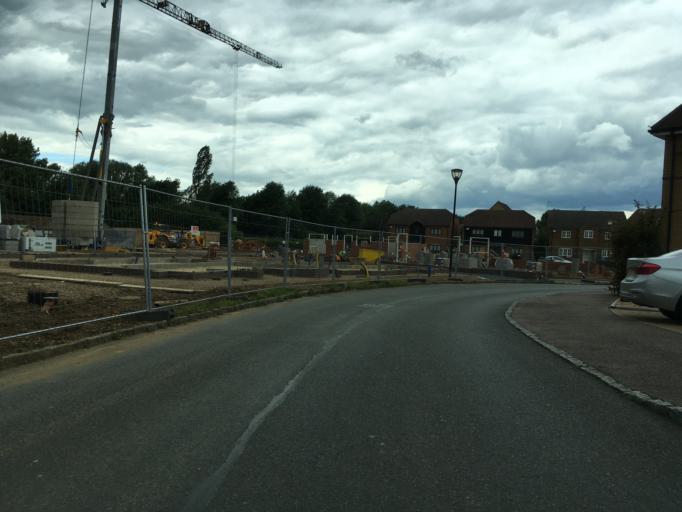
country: GB
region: England
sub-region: Milton Keynes
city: Simpson
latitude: 52.0308
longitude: -0.7105
